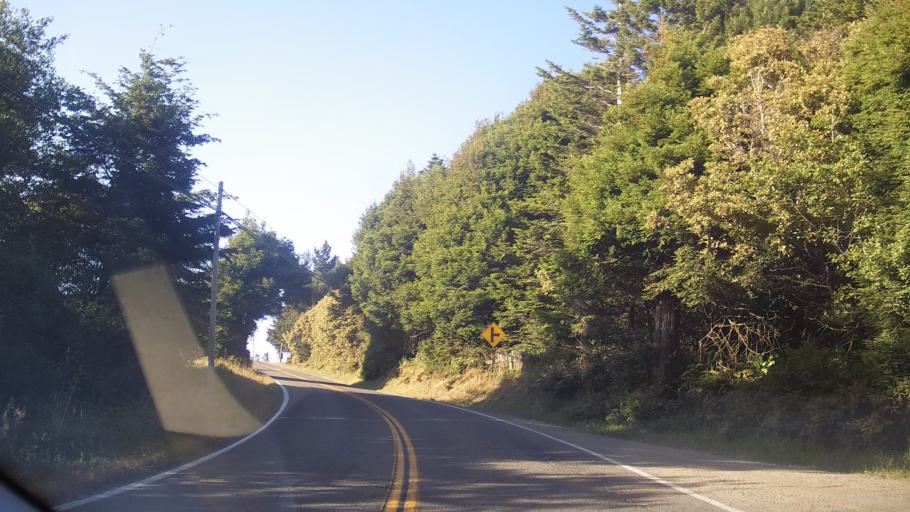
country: US
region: California
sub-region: Mendocino County
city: Fort Bragg
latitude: 39.5094
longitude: -123.7650
